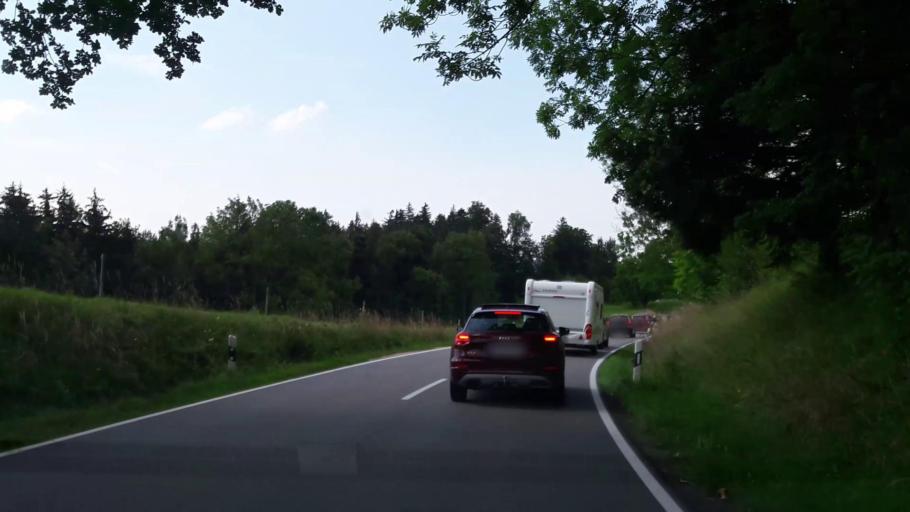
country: DE
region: Bavaria
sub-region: Upper Bavaria
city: Teisendorf
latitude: 47.8310
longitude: 12.8368
